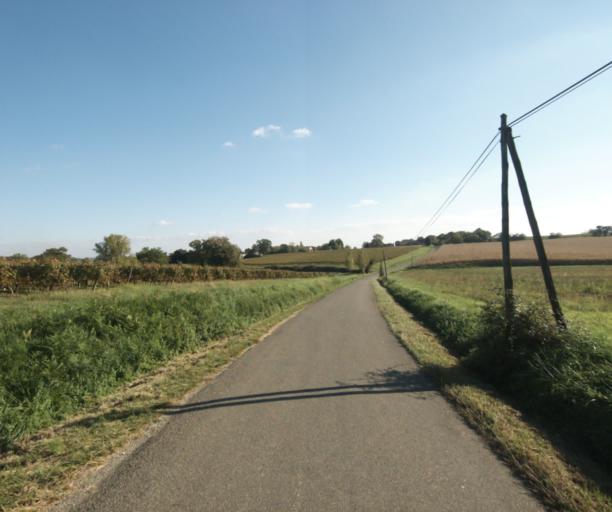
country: FR
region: Midi-Pyrenees
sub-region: Departement du Gers
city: Eauze
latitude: 43.8003
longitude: 0.1346
